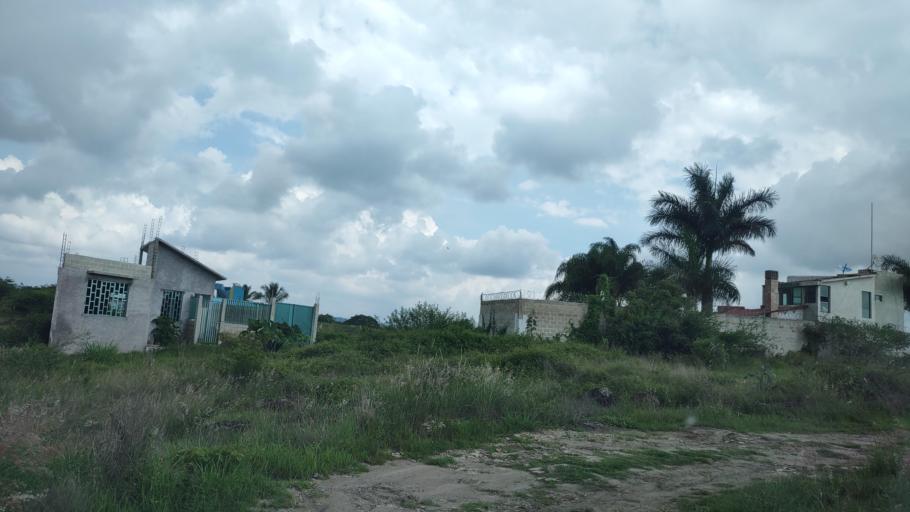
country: MX
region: Veracruz
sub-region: Emiliano Zapata
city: Dos Rios
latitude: 19.4615
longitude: -96.7916
